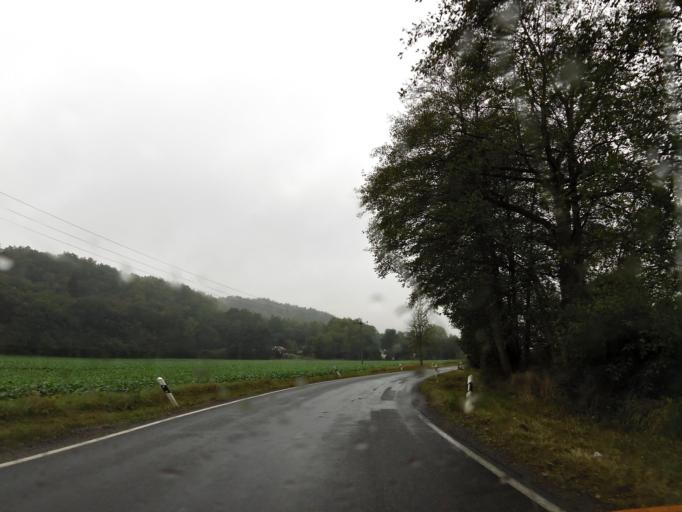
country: DE
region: Thuringia
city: Niedersachswerfen
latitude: 51.5647
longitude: 10.7549
